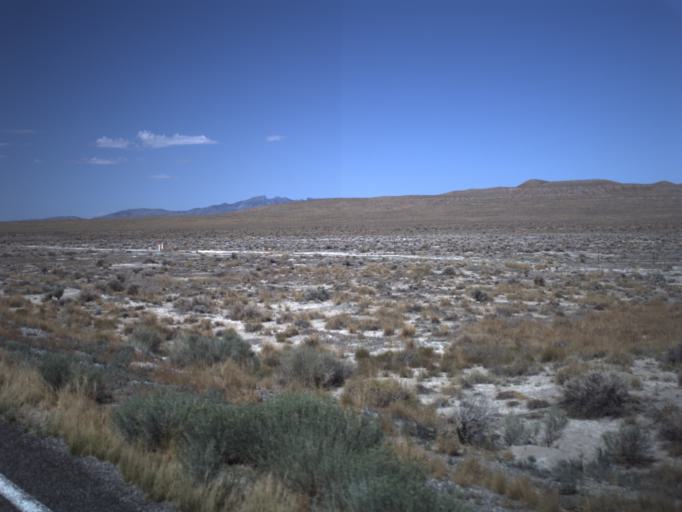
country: US
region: Utah
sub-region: Millard County
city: Delta
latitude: 39.1670
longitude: -113.0405
